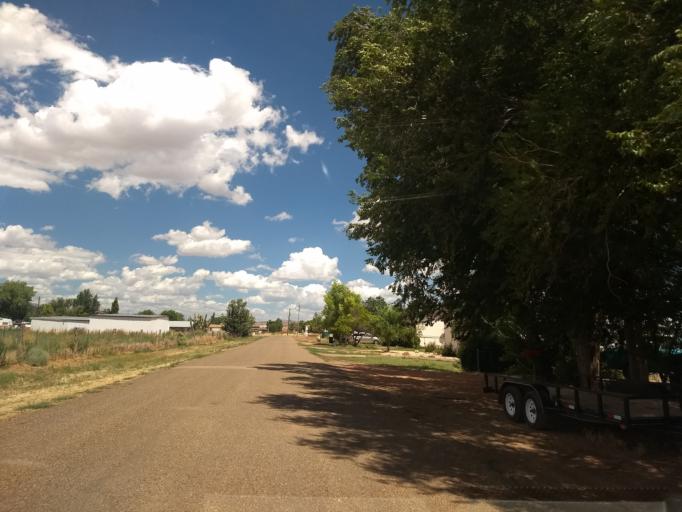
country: US
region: Arizona
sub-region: Coconino County
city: Fredonia
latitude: 36.9440
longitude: -112.5205
